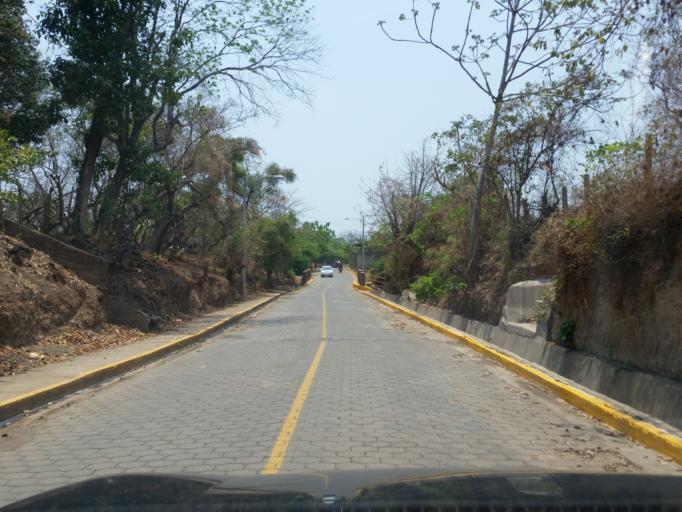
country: NI
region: Granada
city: Granada
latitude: 11.9324
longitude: -85.9721
